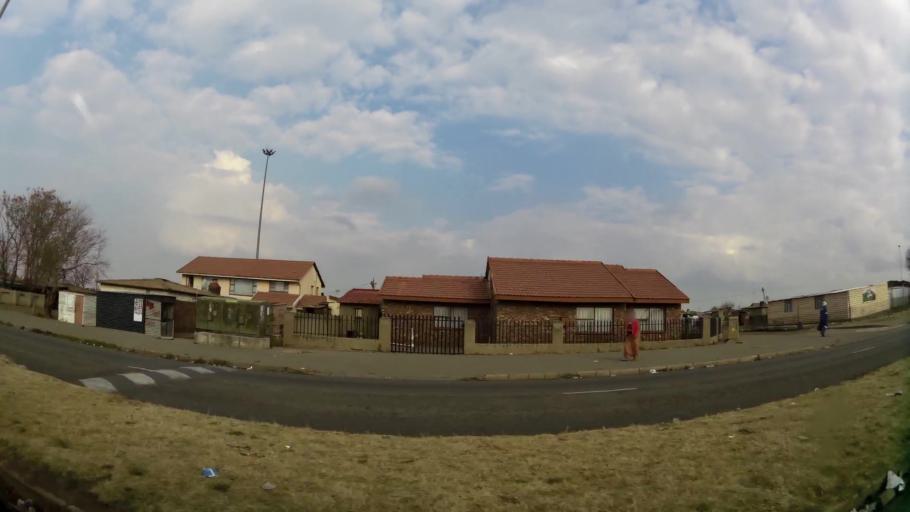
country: ZA
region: Gauteng
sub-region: Sedibeng District Municipality
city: Vereeniging
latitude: -26.6800
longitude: 27.8844
